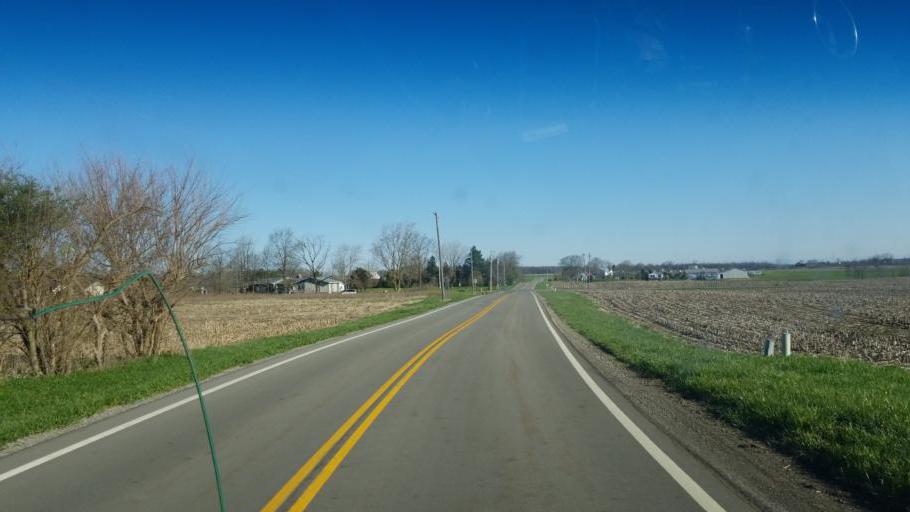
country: US
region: Ohio
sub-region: Logan County
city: Northwood
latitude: 40.4989
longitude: -83.6355
